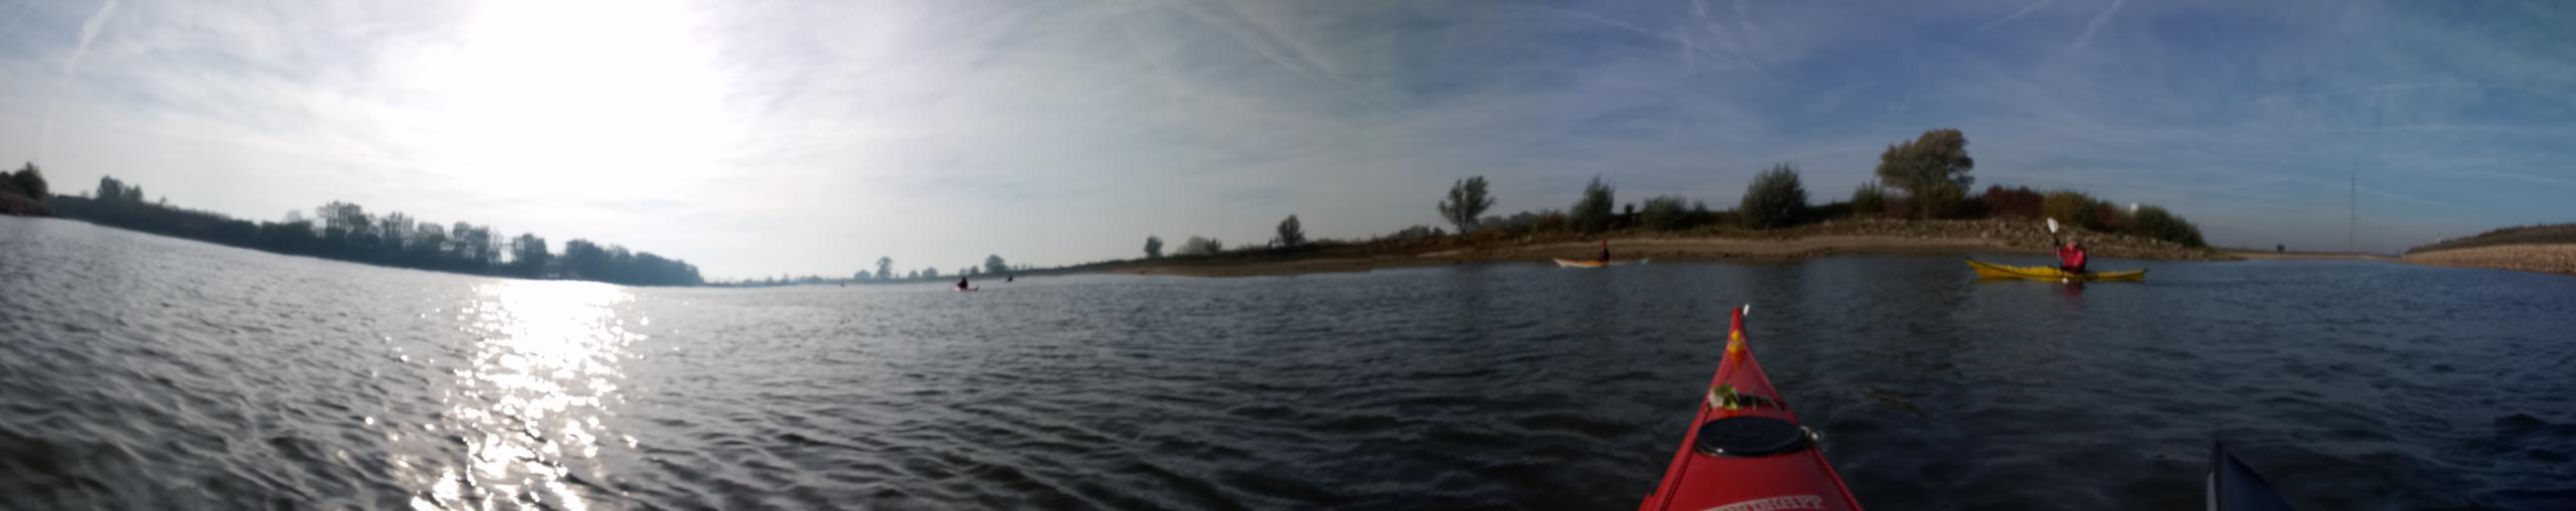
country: NL
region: Gelderland
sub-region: Gemeente Zutphen
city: Zutphen
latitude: 52.1576
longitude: 6.1861
